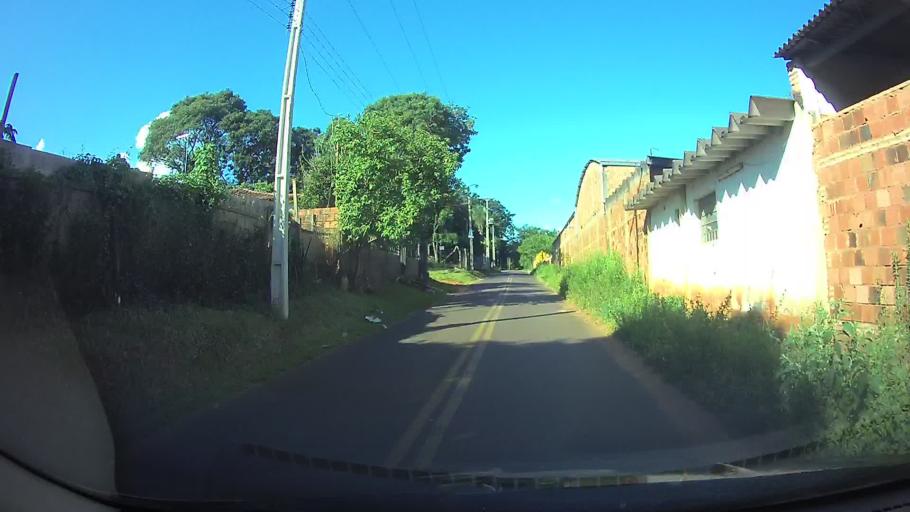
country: PY
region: Central
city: Aregua
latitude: -25.3537
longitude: -57.3947
